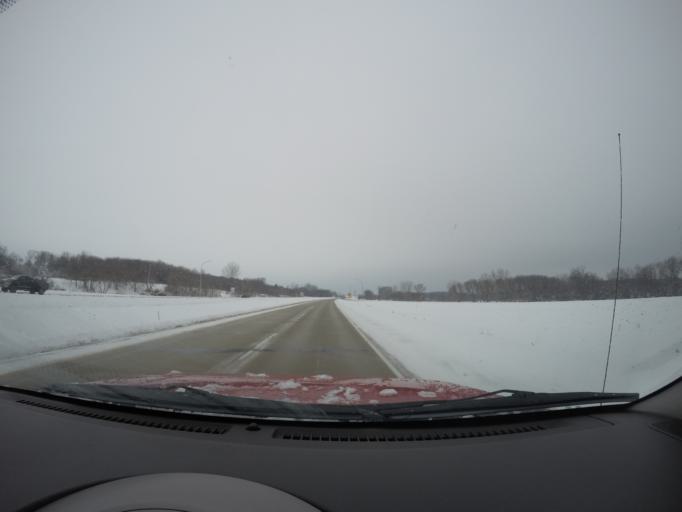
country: US
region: Minnesota
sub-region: Olmsted County
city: Rochester
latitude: 43.9595
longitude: -92.3810
